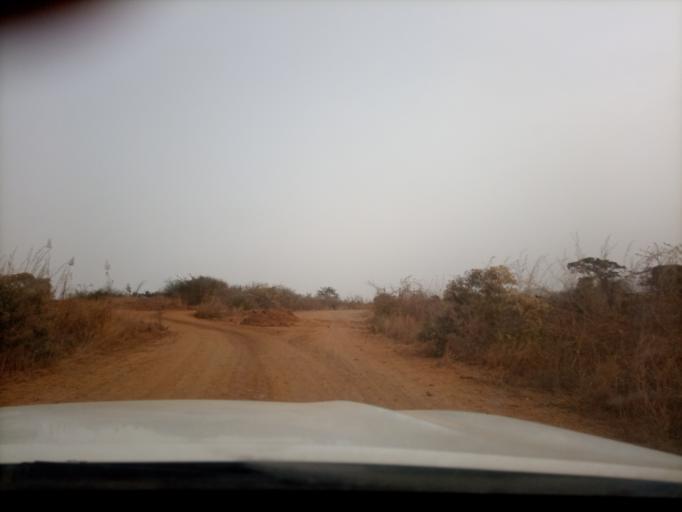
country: ET
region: Oromiya
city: Mendi
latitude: 10.1839
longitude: 35.0475
